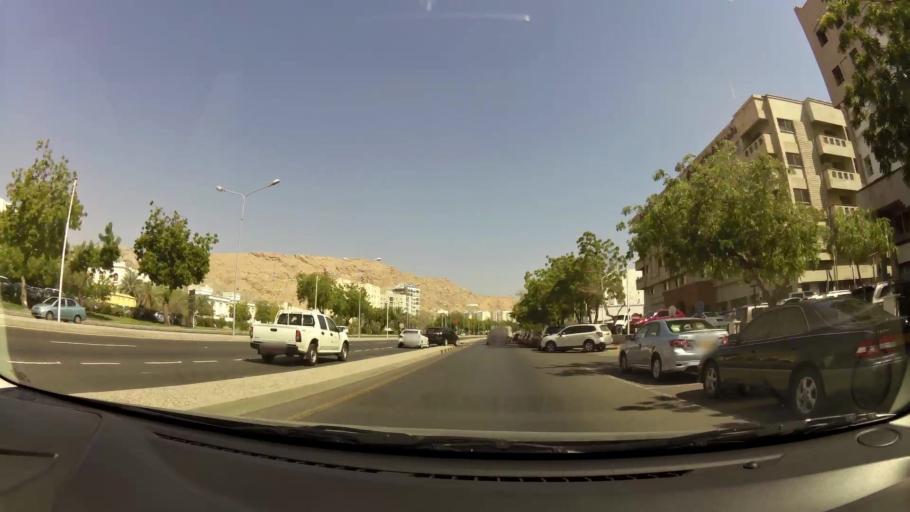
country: OM
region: Muhafazat Masqat
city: Muscat
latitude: 23.5969
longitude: 58.5400
